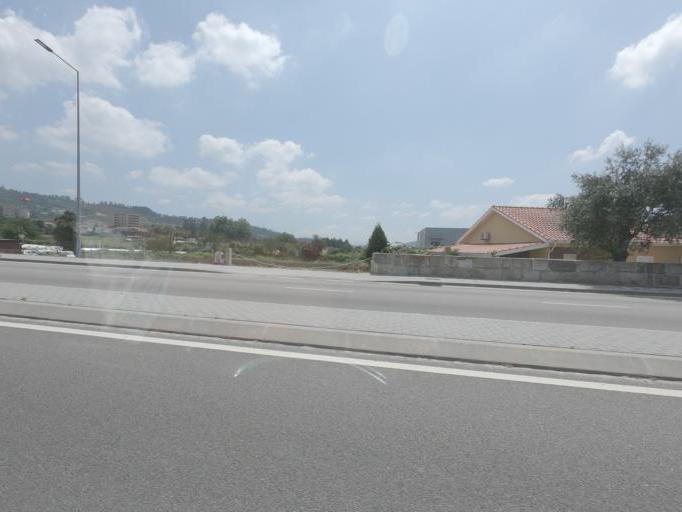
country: PT
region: Porto
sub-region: Penafiel
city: Penafiel
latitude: 41.1937
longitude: -8.3038
